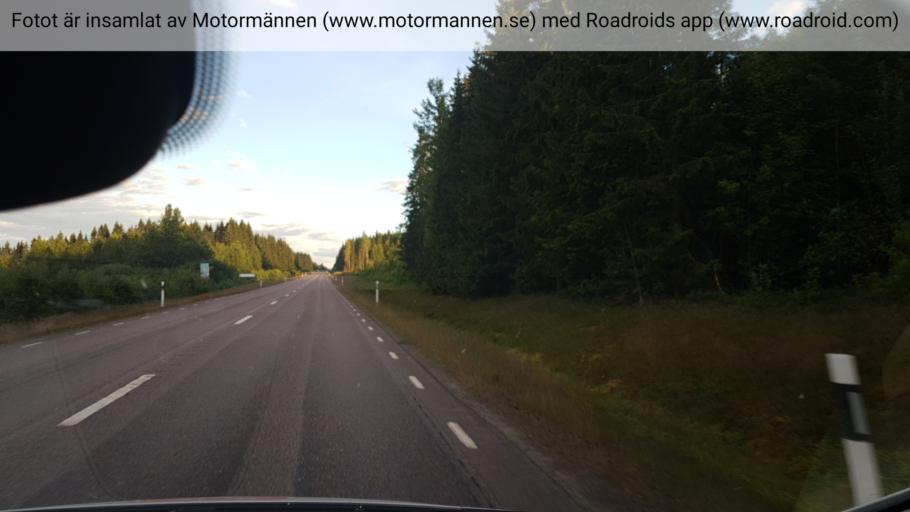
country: SE
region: Vaermland
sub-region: Torsby Kommun
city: Torsby
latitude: 60.0104
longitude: 13.0848
